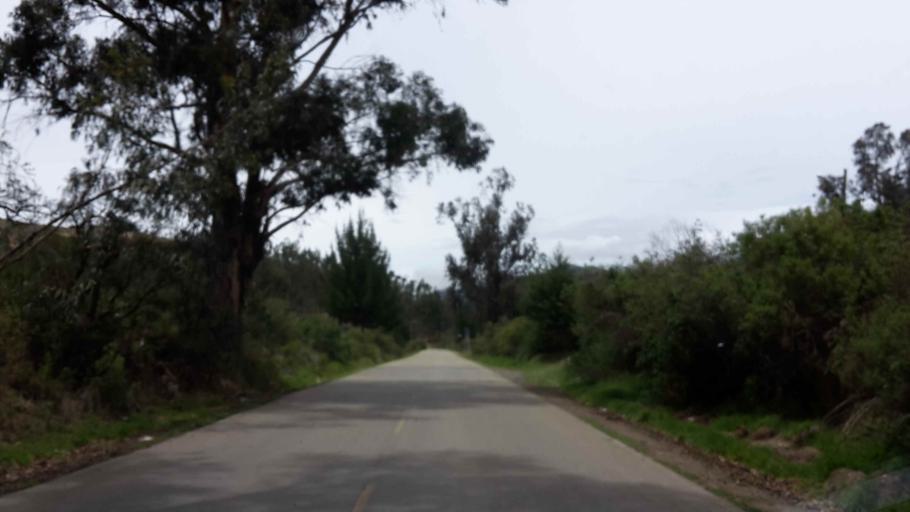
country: BO
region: Cochabamba
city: Totora
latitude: -17.6825
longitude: -65.2151
